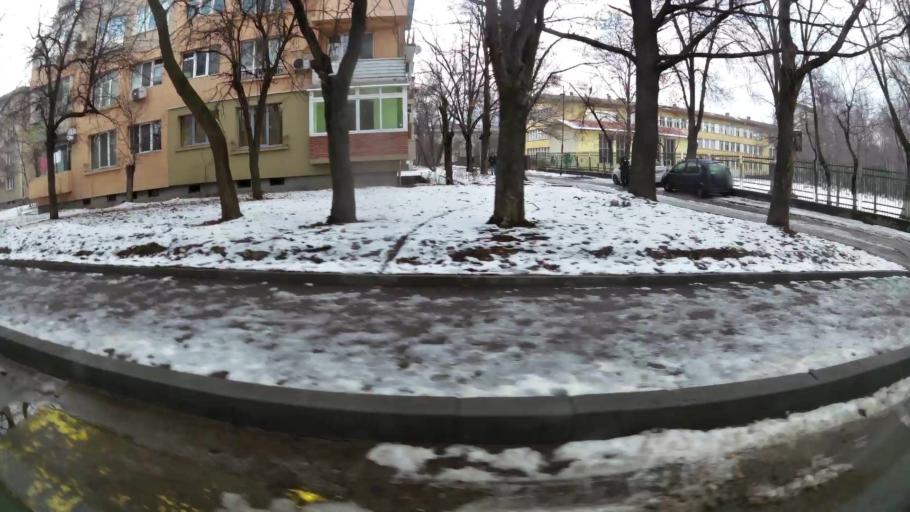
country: BG
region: Sofia-Capital
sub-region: Stolichna Obshtina
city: Sofia
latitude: 42.7043
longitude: 23.2819
